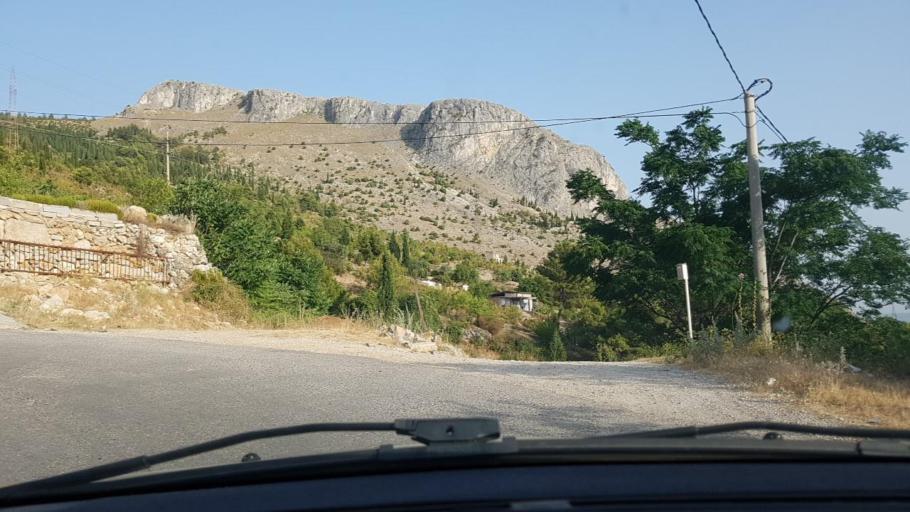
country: BA
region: Federation of Bosnia and Herzegovina
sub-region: Hercegovacko-Bosanski Kanton
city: Mostar
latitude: 43.3484
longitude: 17.8208
